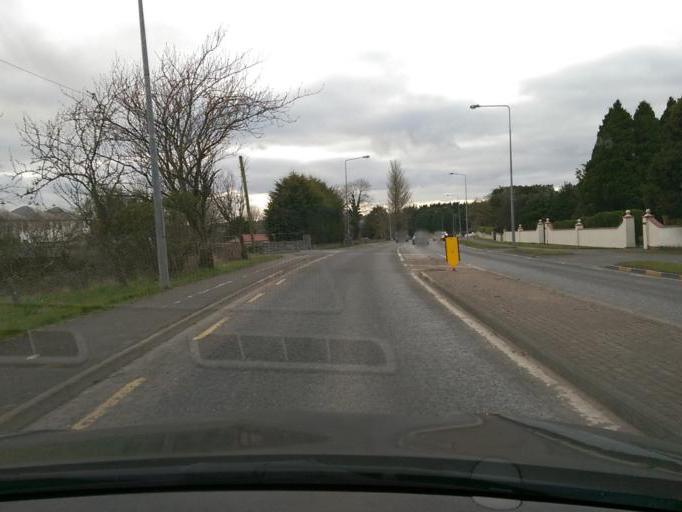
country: IE
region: Leinster
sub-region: An Iarmhi
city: Moate
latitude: 53.3956
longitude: -7.7021
